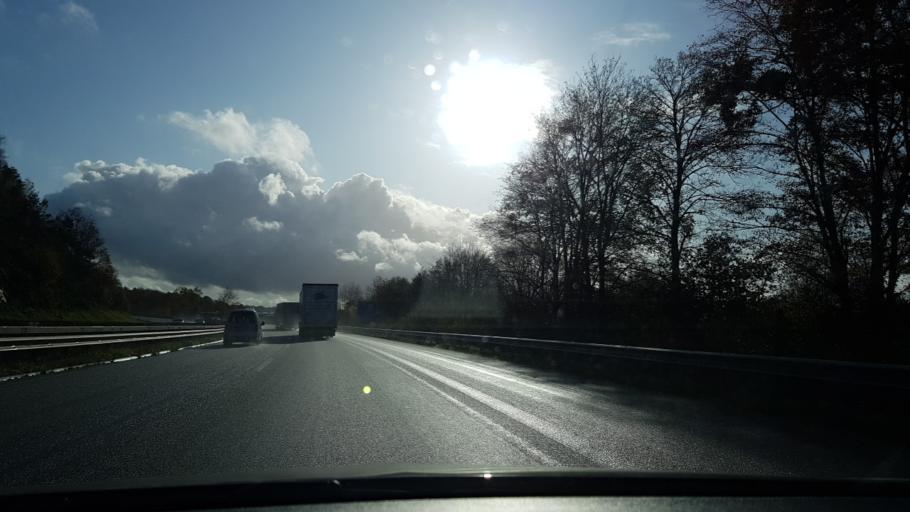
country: DE
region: Rheinland-Pfalz
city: Mehren
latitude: 50.1625
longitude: 6.8825
